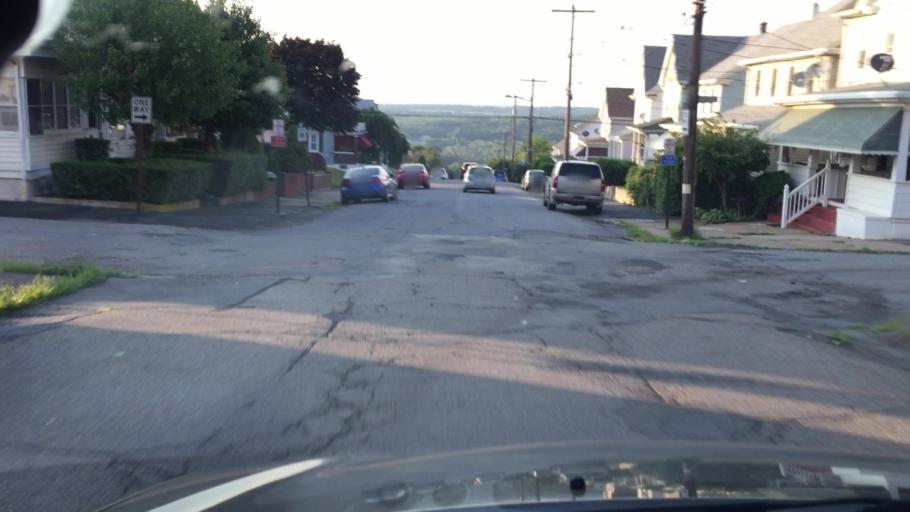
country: US
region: Pennsylvania
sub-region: Luzerne County
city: Hazleton
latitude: 40.9662
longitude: -75.9709
